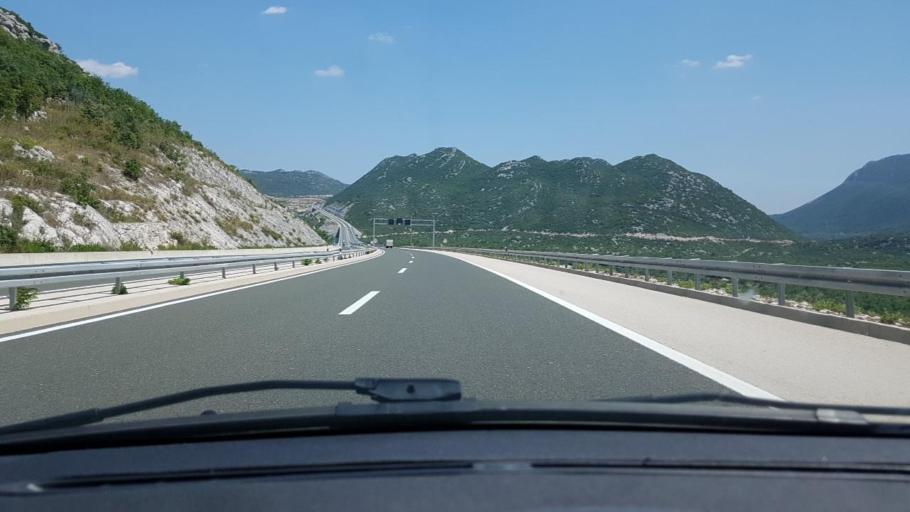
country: HR
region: Splitsko-Dalmatinska
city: Vrgorac
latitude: 43.1949
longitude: 17.3337
